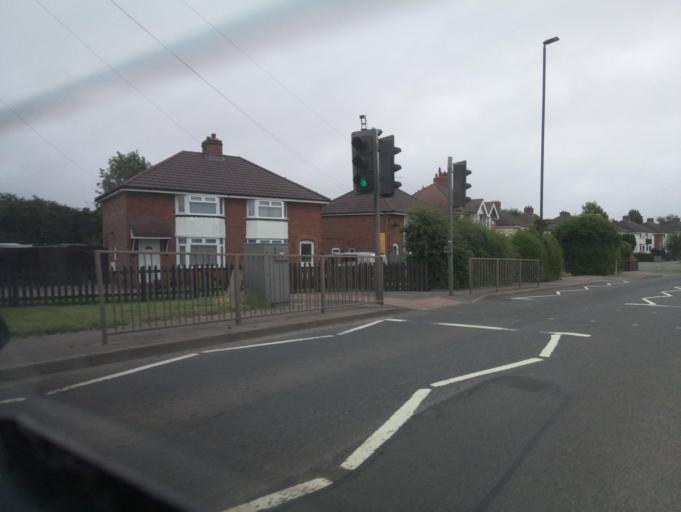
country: GB
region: England
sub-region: Staffordshire
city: Burton upon Trent
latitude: 52.7817
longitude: -1.6089
